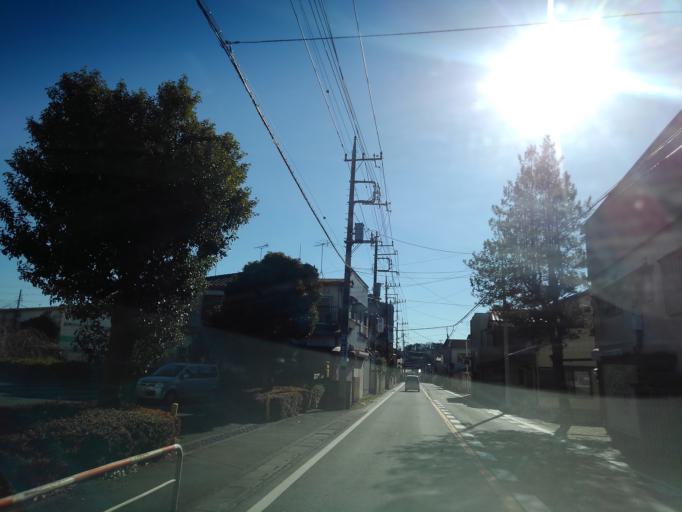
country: JP
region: Saitama
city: Hanno
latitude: 35.8426
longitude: 139.3222
